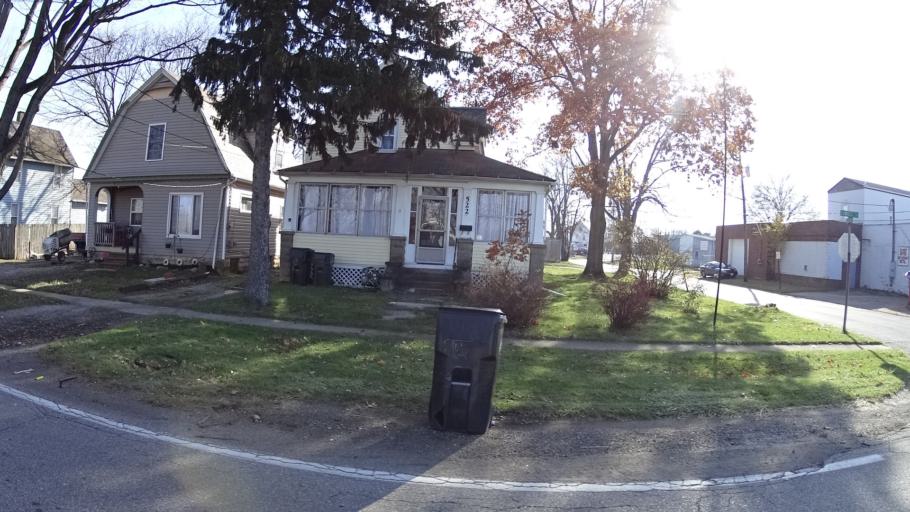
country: US
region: Ohio
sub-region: Lorain County
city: Elyria
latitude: 41.3751
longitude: -82.1239
